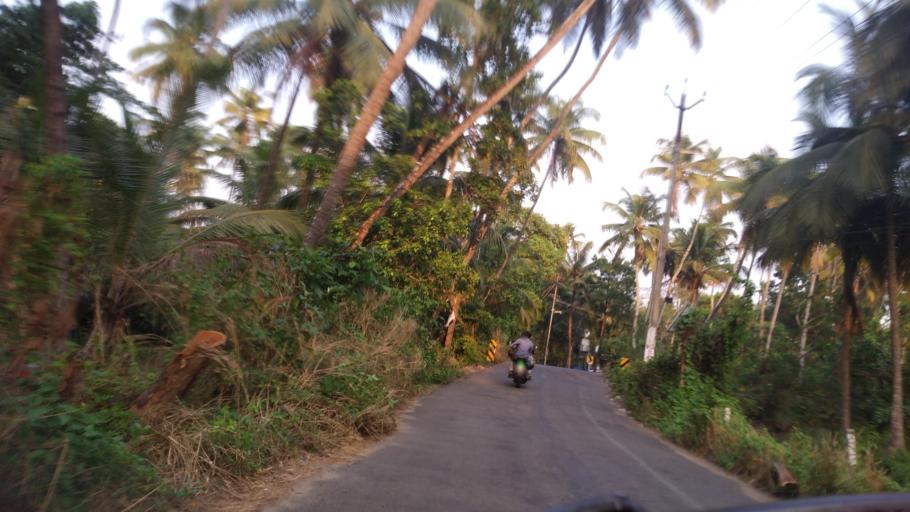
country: IN
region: Kerala
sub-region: Thrissur District
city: Thanniyam
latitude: 10.3460
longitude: 76.1146
